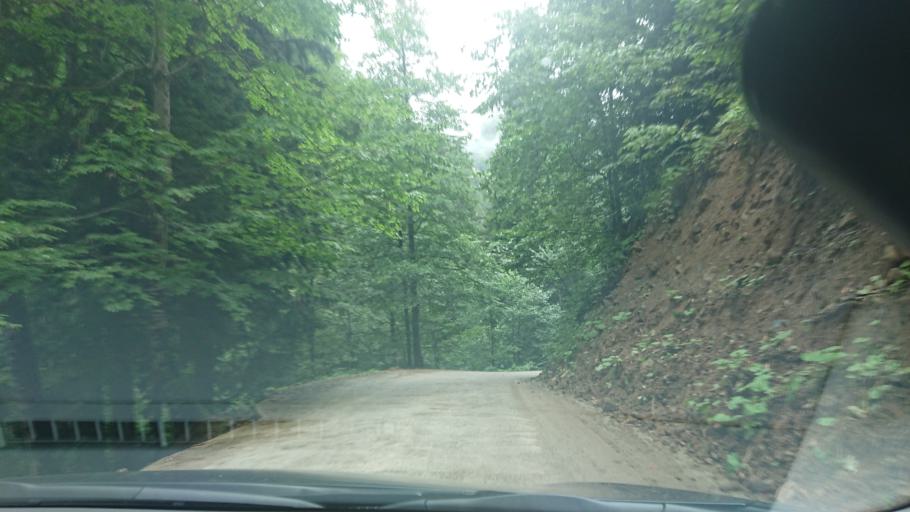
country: TR
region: Gumushane
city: Kurtun
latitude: 40.6665
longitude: 39.0398
